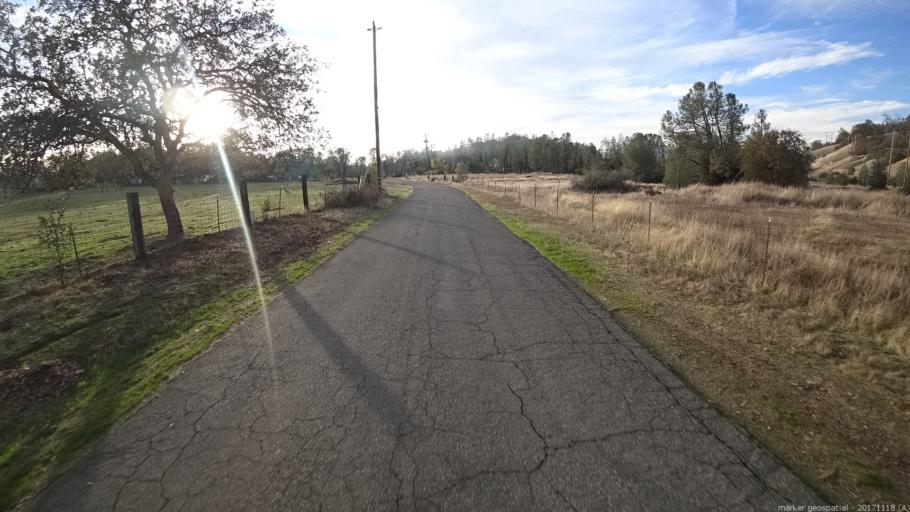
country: US
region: California
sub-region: Shasta County
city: Anderson
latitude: 40.4576
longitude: -122.3411
